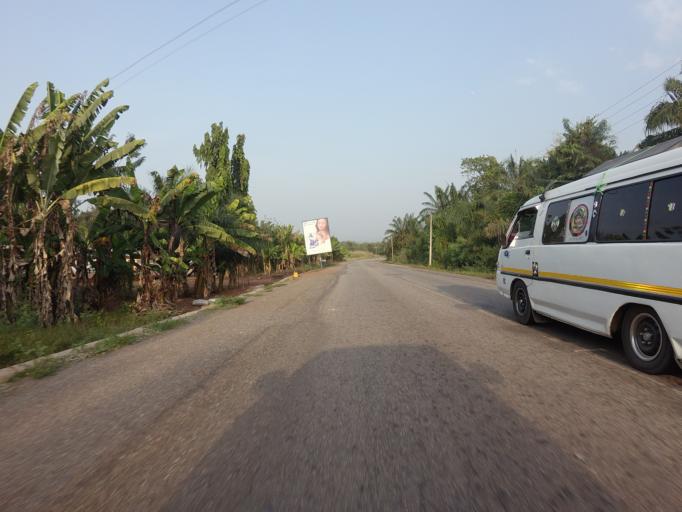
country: GH
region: Volta
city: Ho
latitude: 6.5727
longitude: 0.3077
